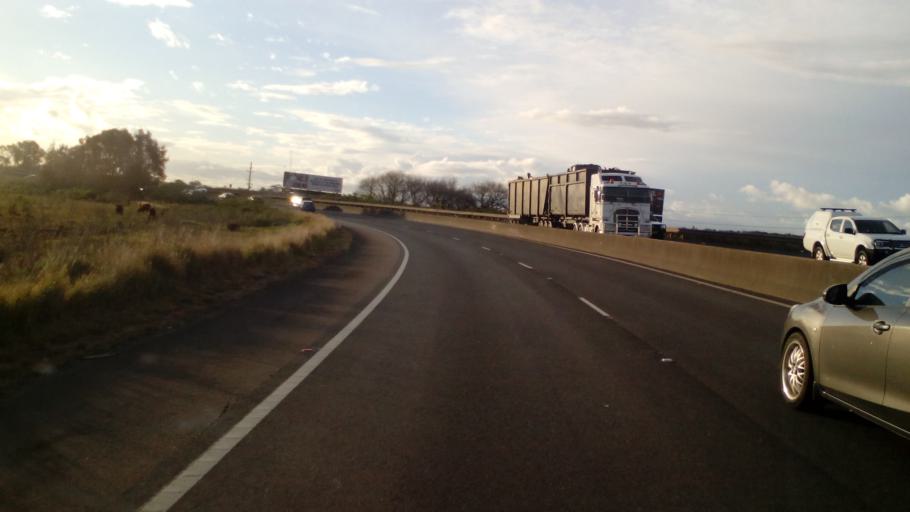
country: AU
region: New South Wales
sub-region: Newcastle
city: Beresfield
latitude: -32.8116
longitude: 151.6750
